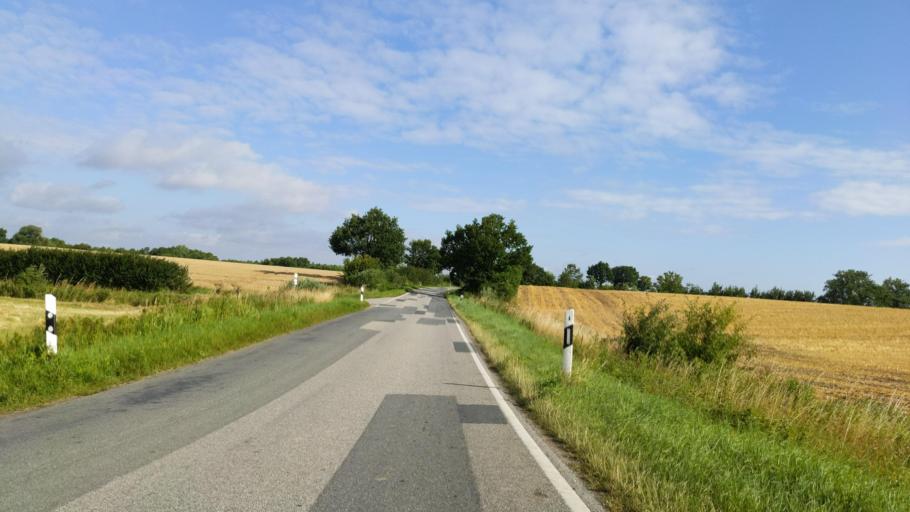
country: DE
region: Schleswig-Holstein
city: Bad Schwartau
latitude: 53.9722
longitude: 10.6559
